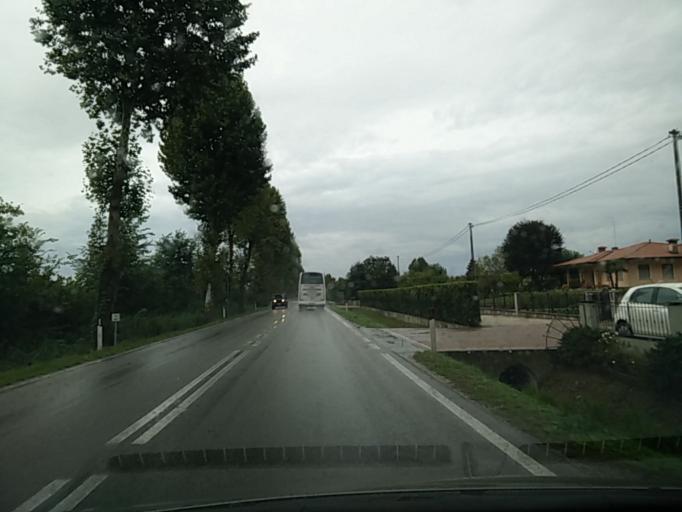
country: IT
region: Veneto
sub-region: Provincia di Treviso
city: Castello di Godego
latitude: 45.6949
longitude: 11.8630
